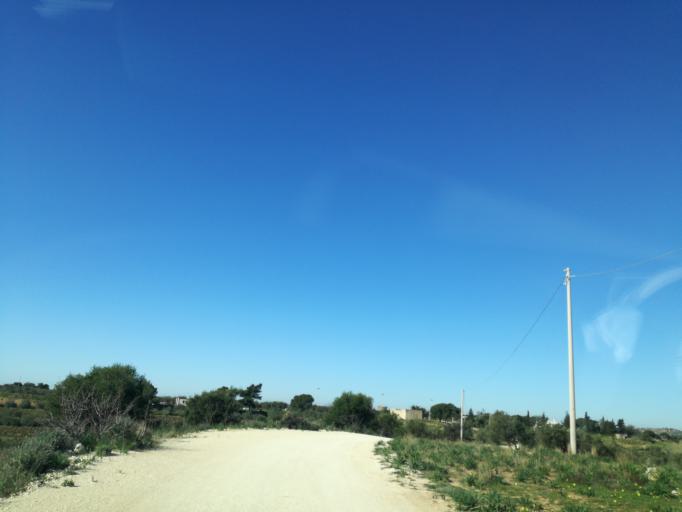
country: IT
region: Sicily
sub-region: Provincia di Caltanissetta
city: Niscemi
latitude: 37.0557
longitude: 14.3618
